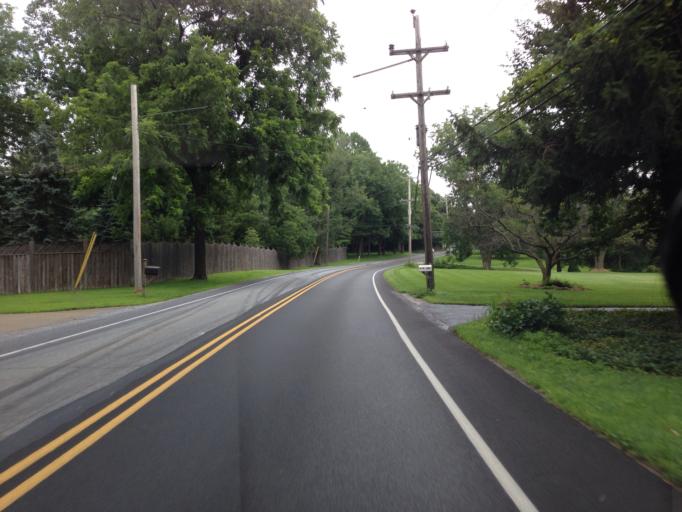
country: US
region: Pennsylvania
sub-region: Chester County
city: West Grove
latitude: 39.7775
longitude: -75.8649
